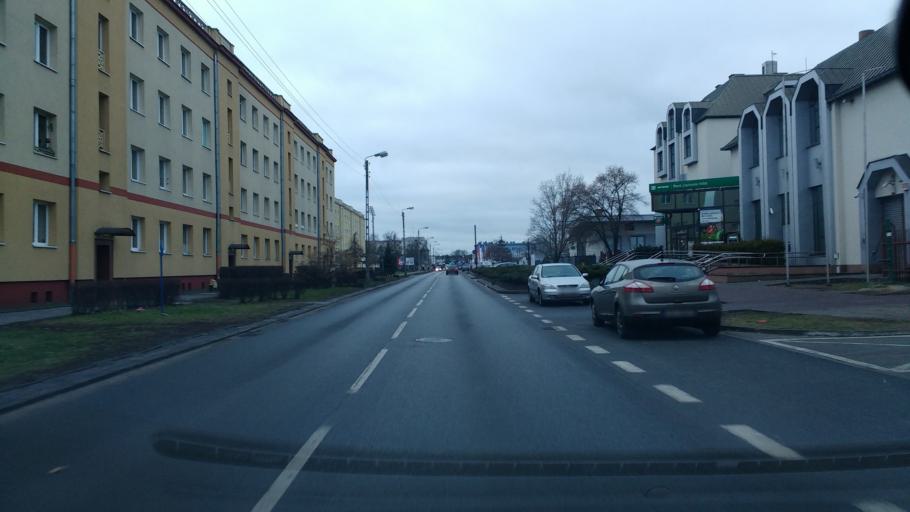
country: PL
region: Kujawsko-Pomorskie
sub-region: Bydgoszcz
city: Bydgoszcz
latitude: 53.1438
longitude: 18.0298
